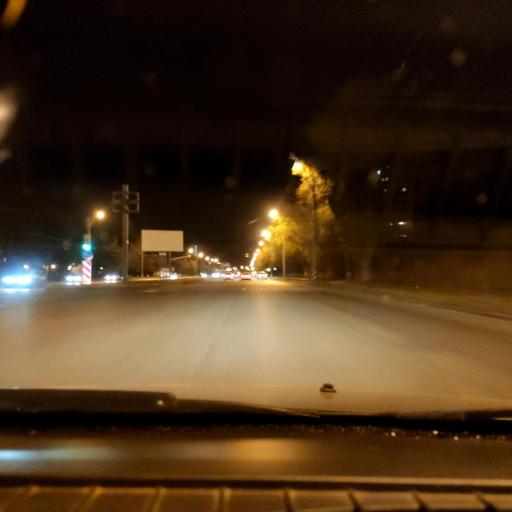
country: RU
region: Samara
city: Tol'yatti
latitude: 53.5168
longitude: 49.2580
